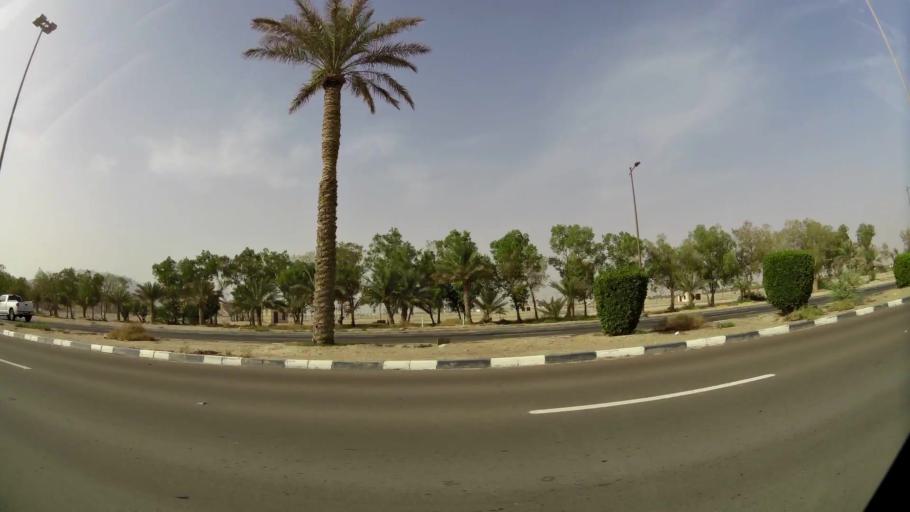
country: AE
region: Abu Dhabi
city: Al Ain
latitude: 24.1337
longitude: 55.7245
